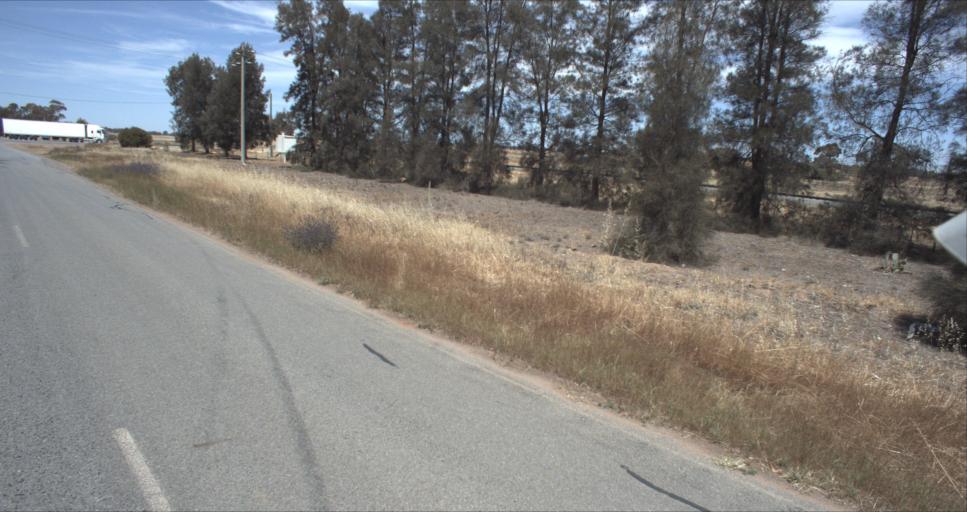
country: AU
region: New South Wales
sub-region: Leeton
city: Leeton
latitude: -34.6460
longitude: 146.4717
